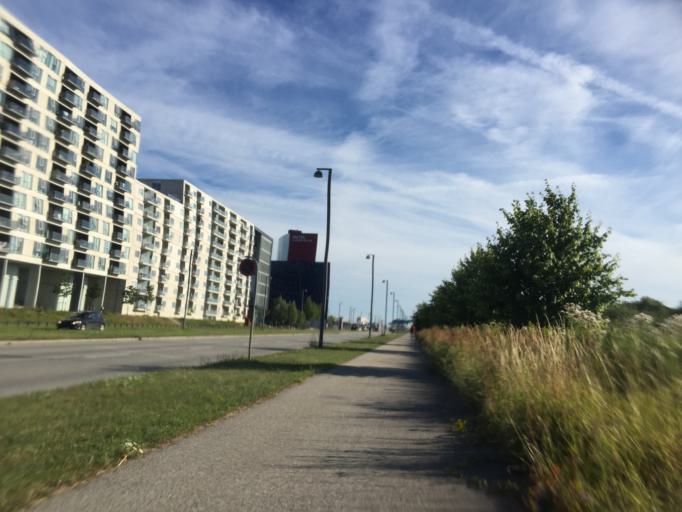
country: DK
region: Capital Region
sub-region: Tarnby Kommune
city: Tarnby
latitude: 55.6335
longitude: 12.5733
